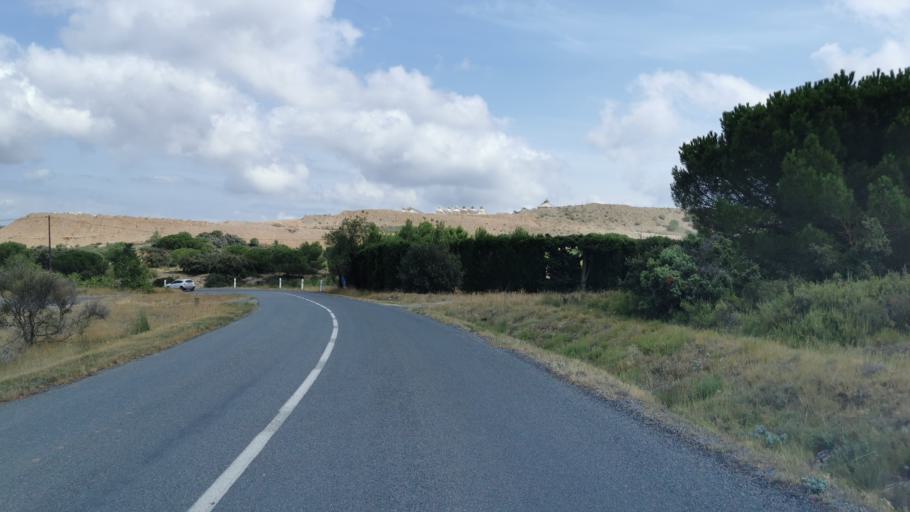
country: FR
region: Languedoc-Roussillon
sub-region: Departement de l'Aude
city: Bizanet
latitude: 43.1621
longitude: 2.8975
